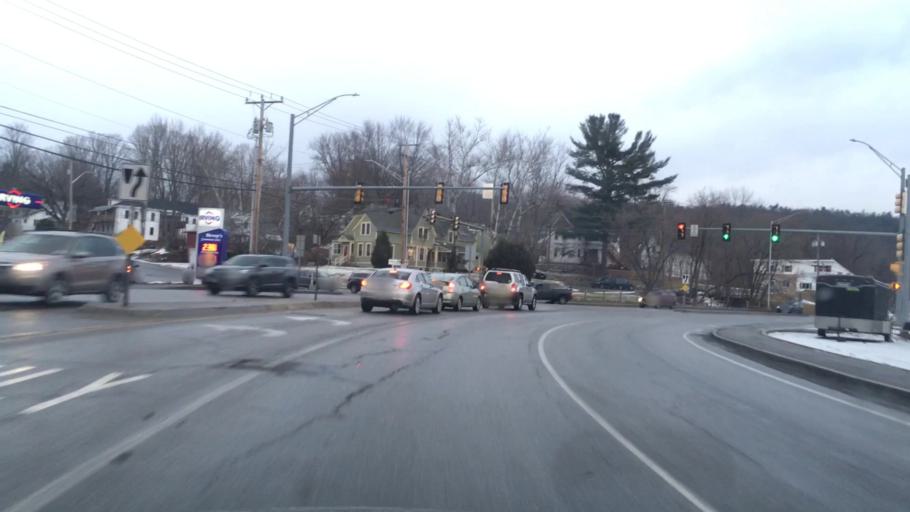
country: US
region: New Hampshire
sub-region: Sullivan County
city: Claremont
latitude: 43.3757
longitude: -72.3341
